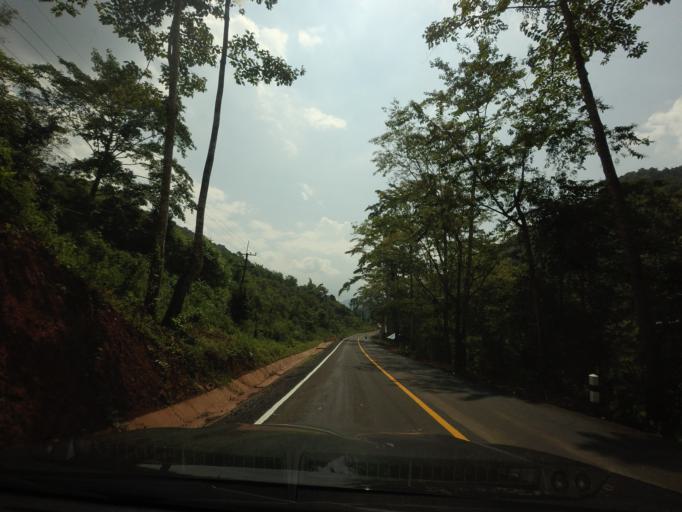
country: TH
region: Nan
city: Bo Kluea
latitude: 19.1775
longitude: 101.1718
